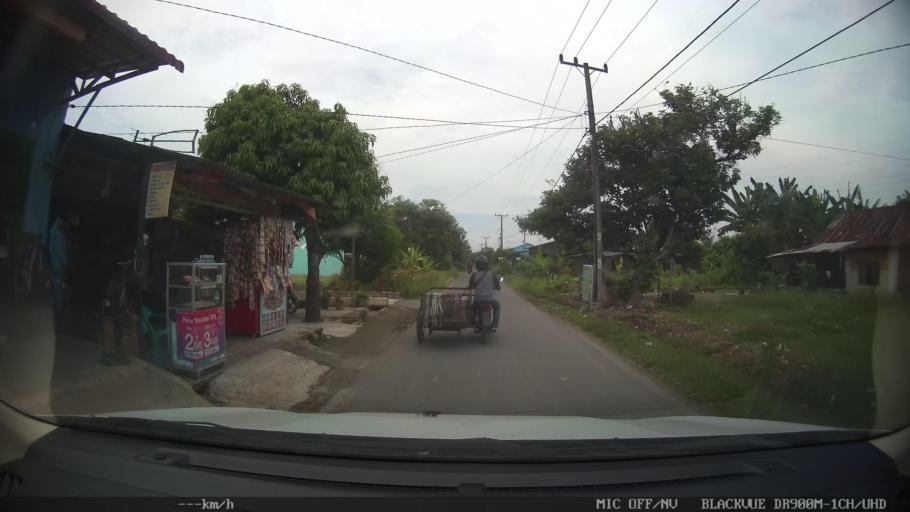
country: ID
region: North Sumatra
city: Sunggal
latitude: 3.6232
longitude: 98.5904
